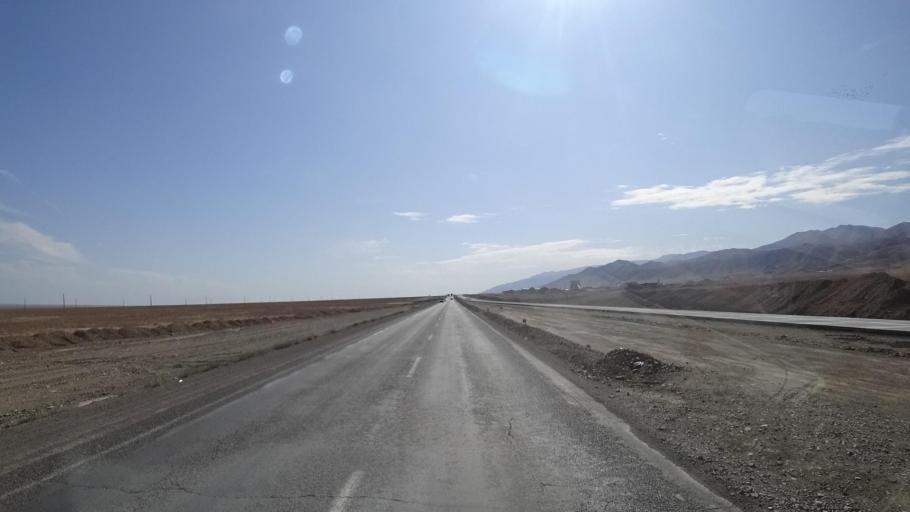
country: KG
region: Chuy
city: Ivanovka
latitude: 43.3941
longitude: 75.1317
